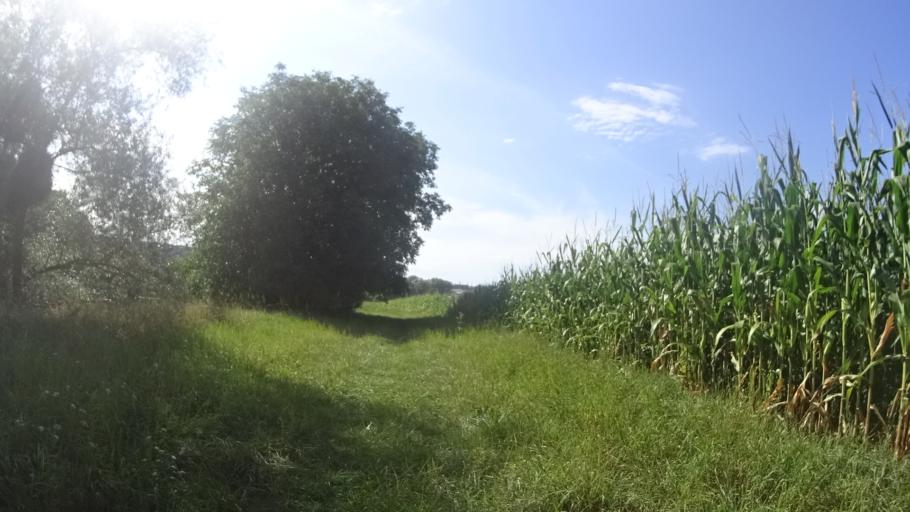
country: FR
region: Franche-Comte
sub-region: Departement du Doubs
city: Thise
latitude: 47.2615
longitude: 6.0759
